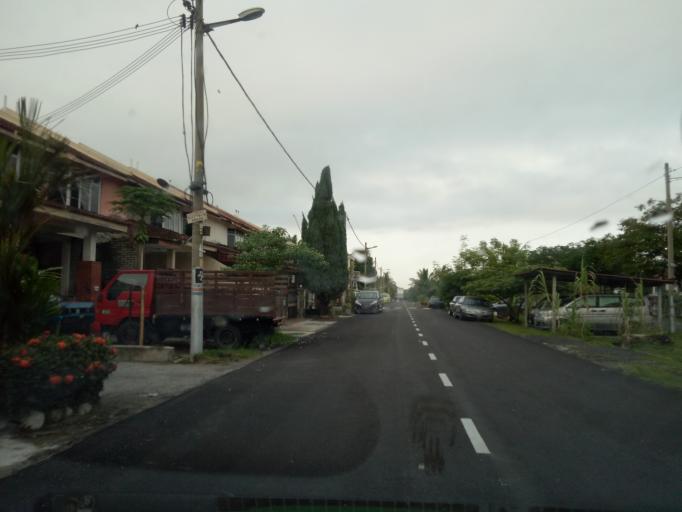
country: MY
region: Selangor
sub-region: Hulu Langat
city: Semenyih
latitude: 2.9314
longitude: 101.8616
